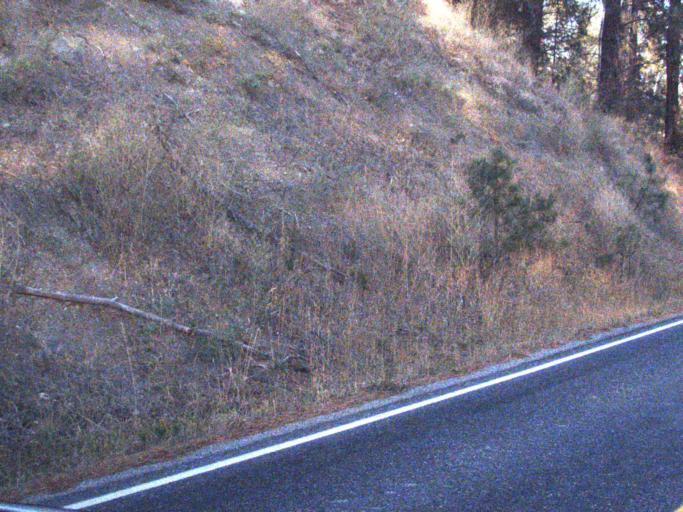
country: US
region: Washington
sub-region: Stevens County
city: Kettle Falls
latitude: 48.7241
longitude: -118.0387
